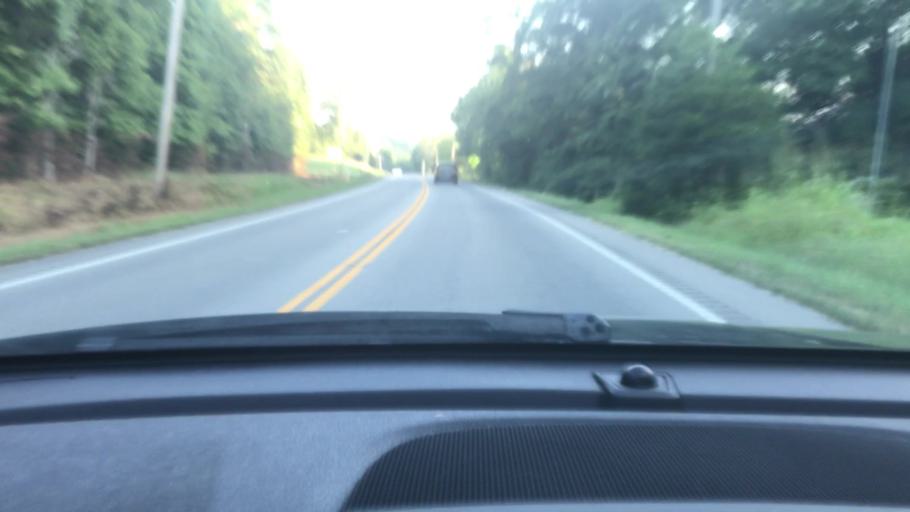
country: US
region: Tennessee
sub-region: Dickson County
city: Charlotte
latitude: 36.1405
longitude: -87.3579
